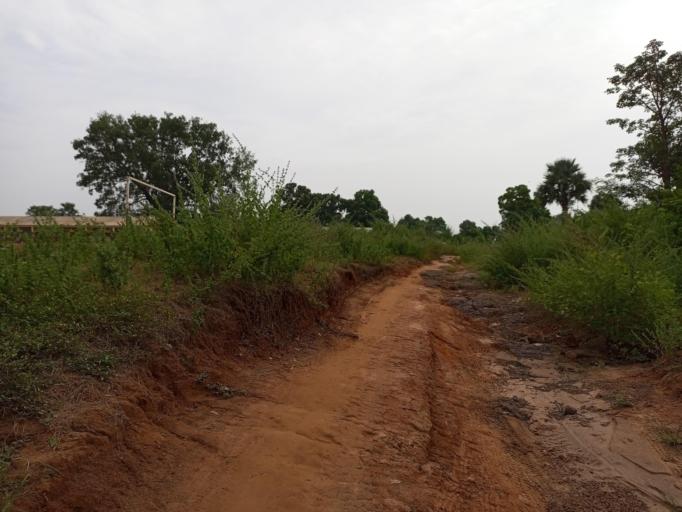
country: GW
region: Oio
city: Bissora
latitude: 12.4601
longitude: -15.4725
